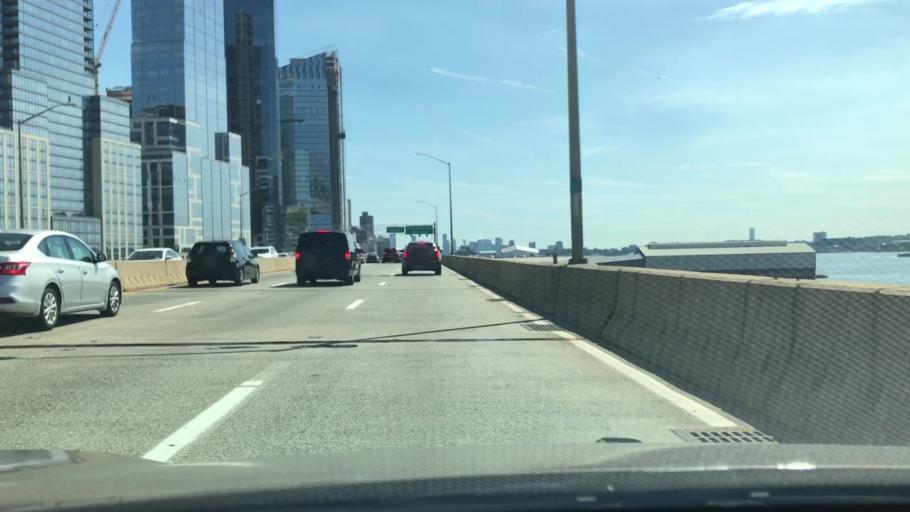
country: US
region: New Jersey
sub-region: Hudson County
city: Guttenberg
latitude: 40.7770
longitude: -73.9906
